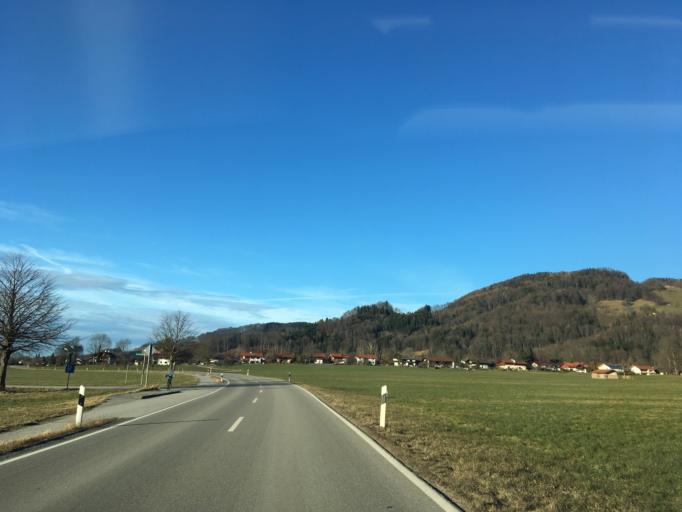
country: DE
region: Bavaria
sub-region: Upper Bavaria
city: Nussdorf am Inn
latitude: 47.7346
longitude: 12.1604
